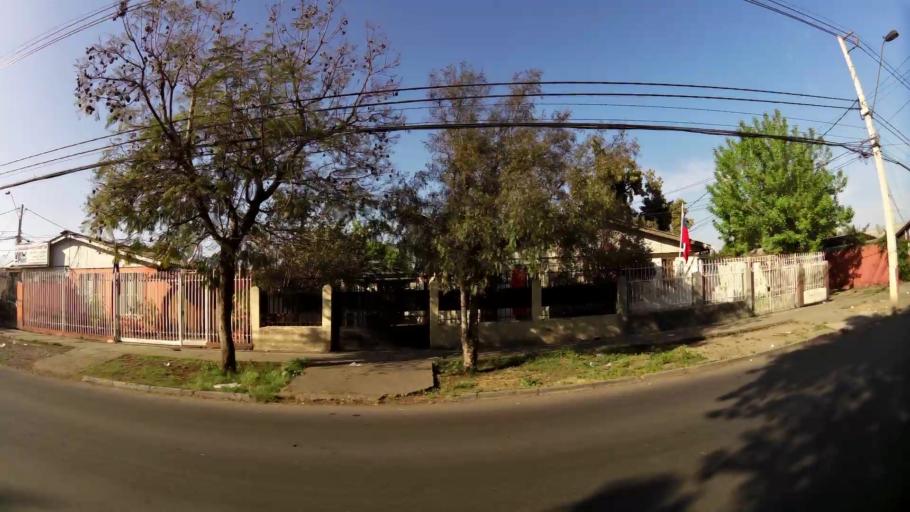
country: CL
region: Santiago Metropolitan
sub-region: Provincia de Santiago
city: Santiago
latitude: -33.3839
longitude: -70.6636
